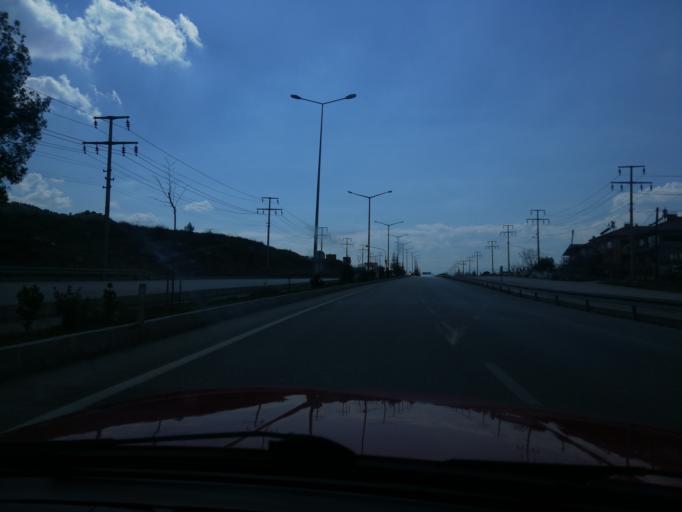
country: TR
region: Burdur
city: Burdur
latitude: 37.7512
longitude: 30.3310
